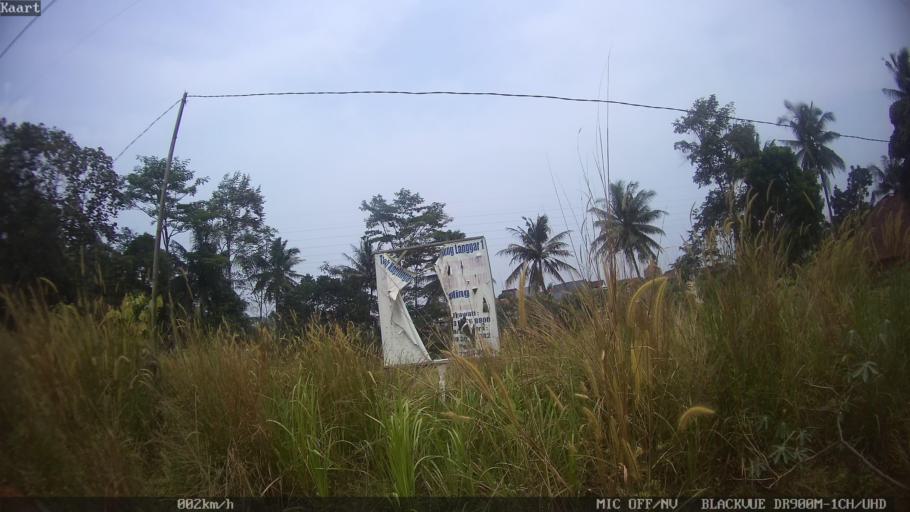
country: ID
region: Lampung
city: Kedaton
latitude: -5.3999
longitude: 105.3263
